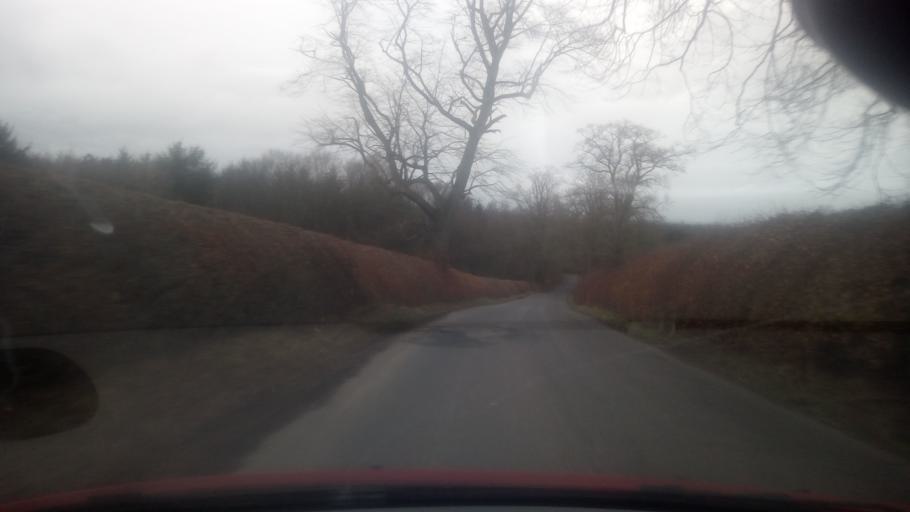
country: GB
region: Scotland
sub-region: The Scottish Borders
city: Jedburgh
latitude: 55.4770
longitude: -2.5247
